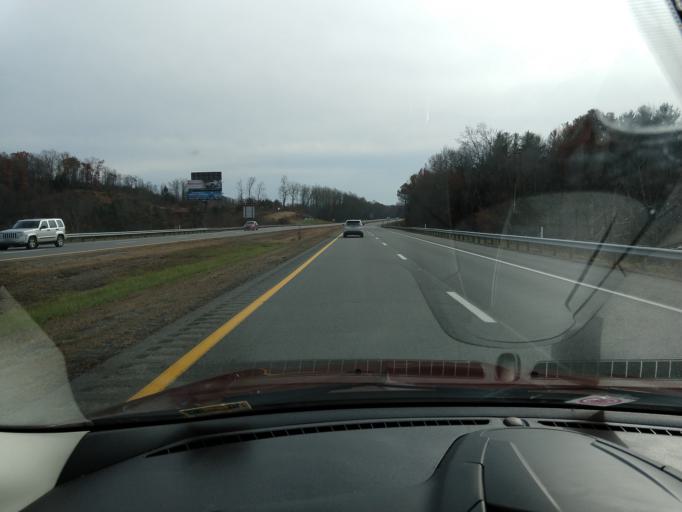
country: US
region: West Virginia
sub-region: Nicholas County
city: Summersville
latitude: 38.2913
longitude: -80.8326
